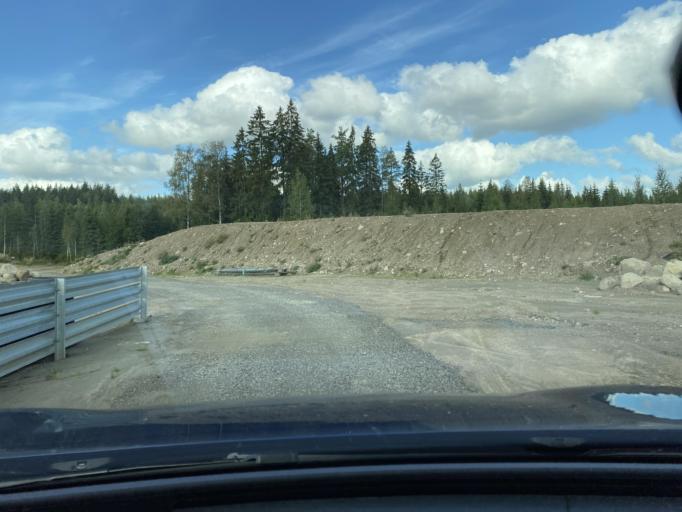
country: FI
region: Kymenlaakso
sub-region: Kouvola
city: Iitti
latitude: 60.8848
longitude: 26.4763
